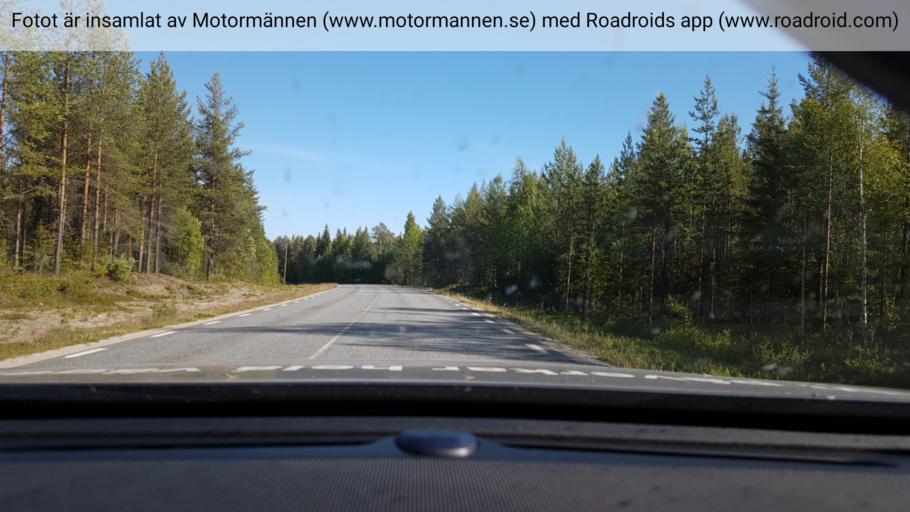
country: SE
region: Vaesterbotten
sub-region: Lycksele Kommun
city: Lycksele
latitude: 64.4594
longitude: 18.9033
